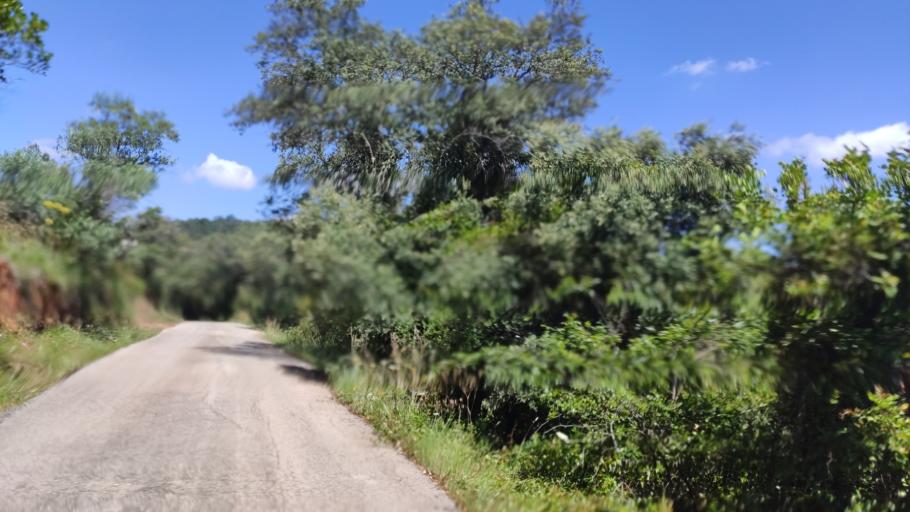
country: PT
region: Faro
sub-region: Sao Bras de Alportel
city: Sao Bras de Alportel
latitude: 37.1719
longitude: -7.9138
